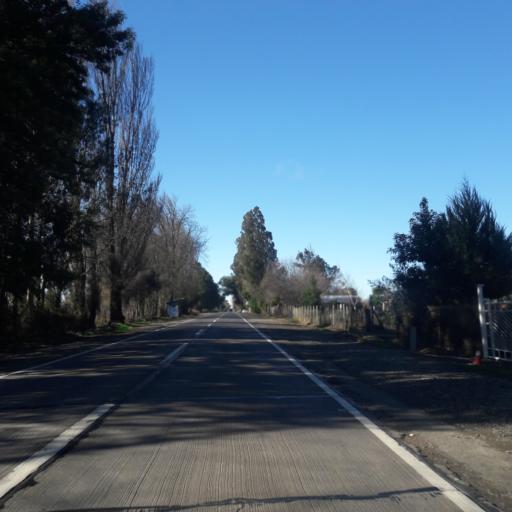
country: CL
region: Araucania
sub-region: Provincia de Malleco
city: Angol
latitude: -37.7604
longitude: -72.5705
